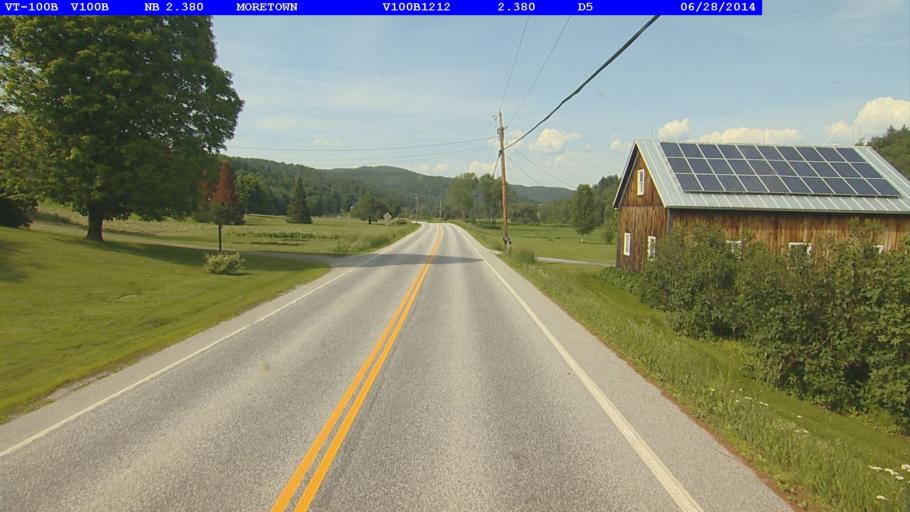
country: US
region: Vermont
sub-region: Washington County
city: Waterbury
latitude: 44.2637
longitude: -72.7474
